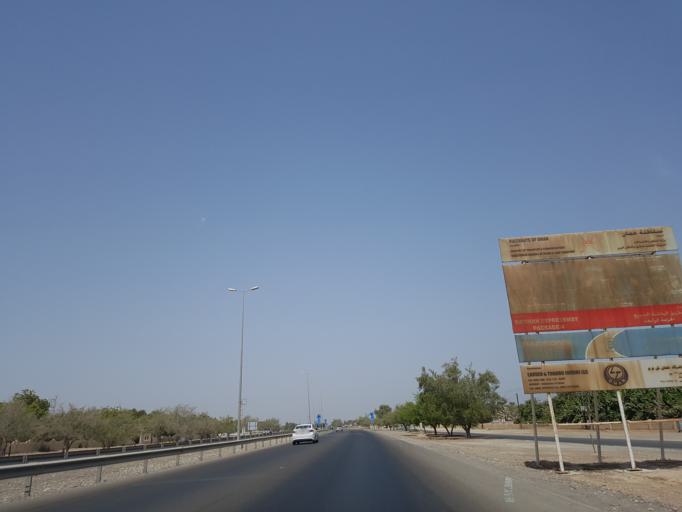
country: OM
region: Al Batinah
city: Al Khaburah
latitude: 24.0453
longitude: 56.9947
